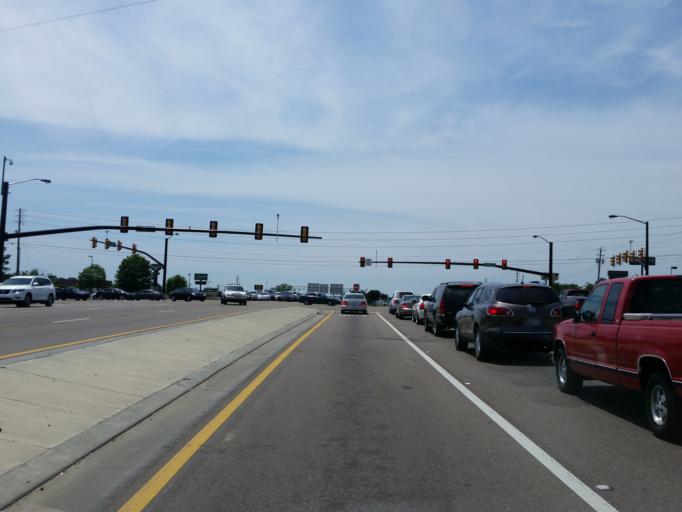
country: US
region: Mississippi
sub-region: Lamar County
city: West Hattiesburg
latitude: 31.3246
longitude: -89.3556
